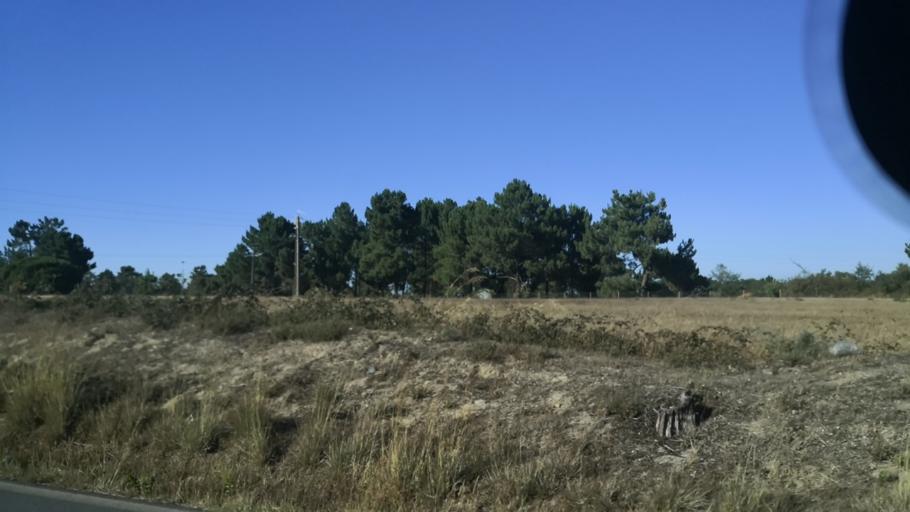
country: PT
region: Setubal
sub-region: Palmela
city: Pinhal Novo
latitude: 38.6190
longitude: -8.9559
